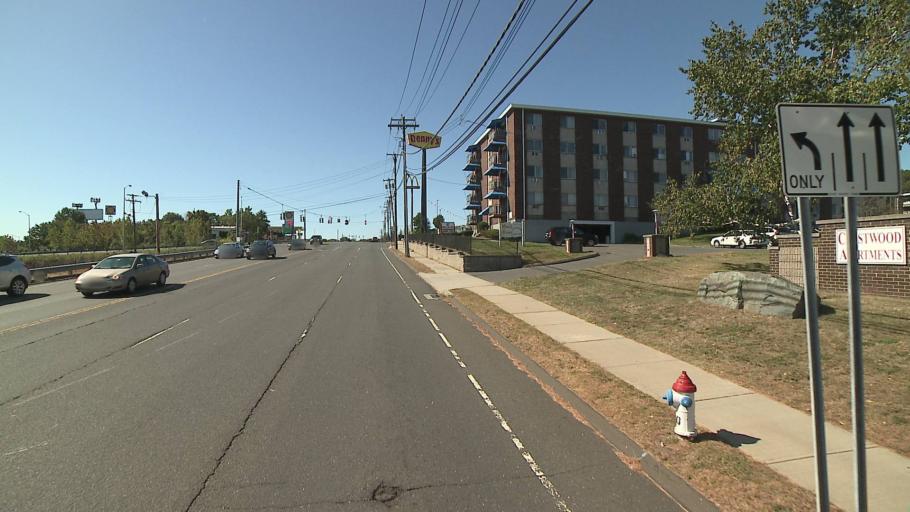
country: US
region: Connecticut
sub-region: New Haven County
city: West Haven
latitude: 41.2718
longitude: -72.9730
